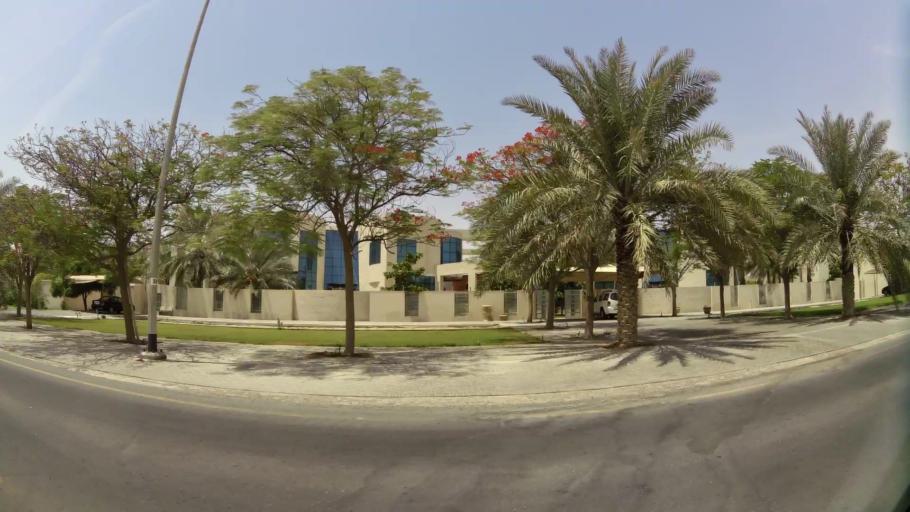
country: AE
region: Ash Shariqah
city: Sharjah
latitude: 25.2347
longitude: 55.4804
